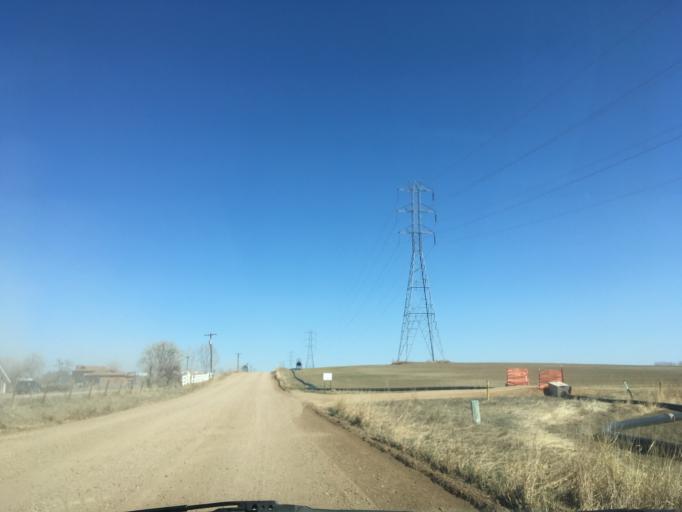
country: US
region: Colorado
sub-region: Boulder County
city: Erie
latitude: 40.0584
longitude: -105.0148
